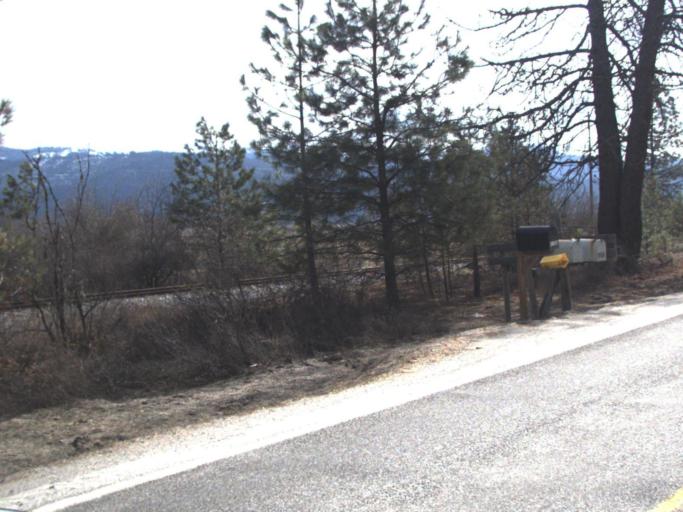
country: US
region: Washington
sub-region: Pend Oreille County
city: Newport
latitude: 48.4344
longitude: -117.3216
